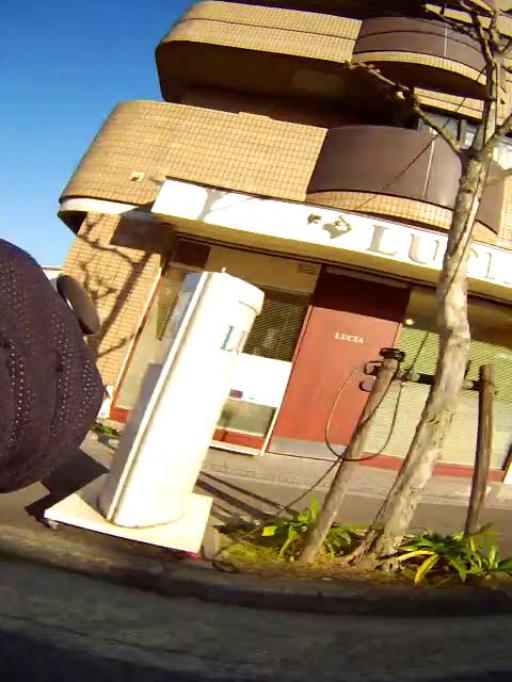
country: JP
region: Hyogo
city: Takarazuka
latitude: 34.7899
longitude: 135.3572
